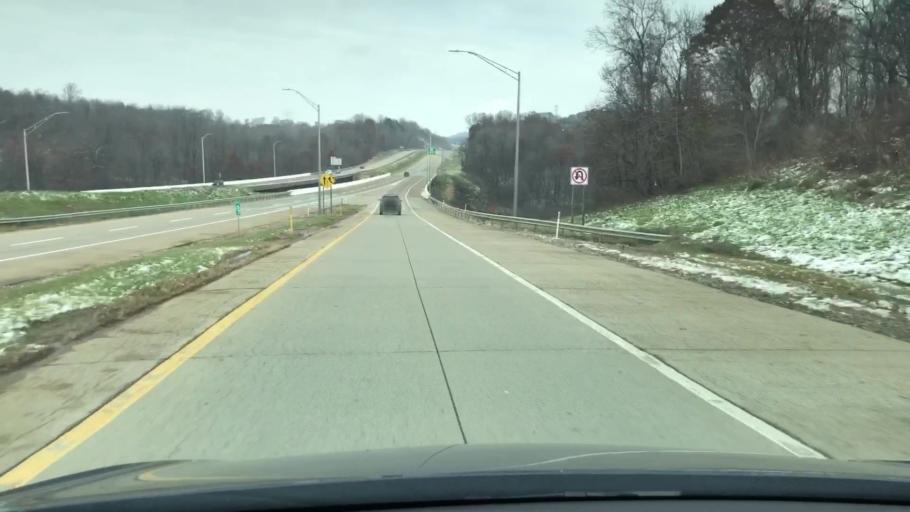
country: US
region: Pennsylvania
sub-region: Westmoreland County
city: Jeannette
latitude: 40.3118
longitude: -79.5915
